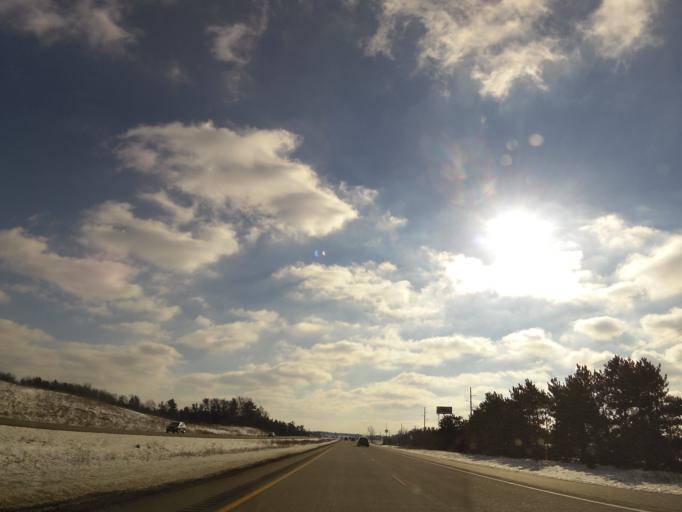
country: US
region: Wisconsin
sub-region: Monroe County
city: Tomah
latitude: 44.0758
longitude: -90.5233
